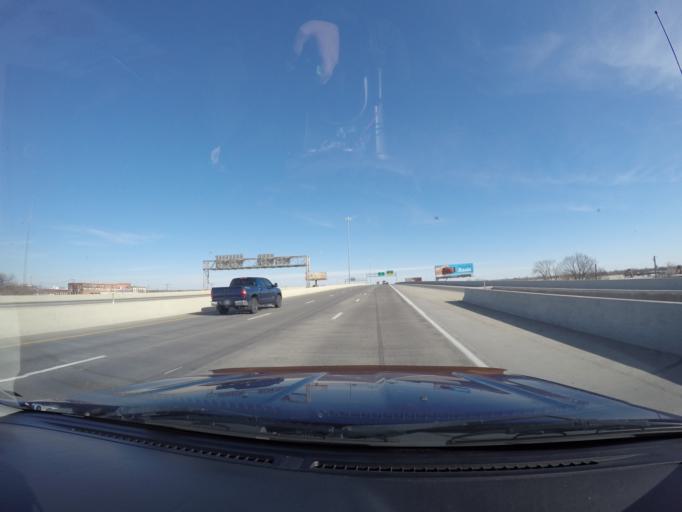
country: US
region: Kansas
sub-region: Sedgwick County
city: Wichita
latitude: 37.6787
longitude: -97.3320
